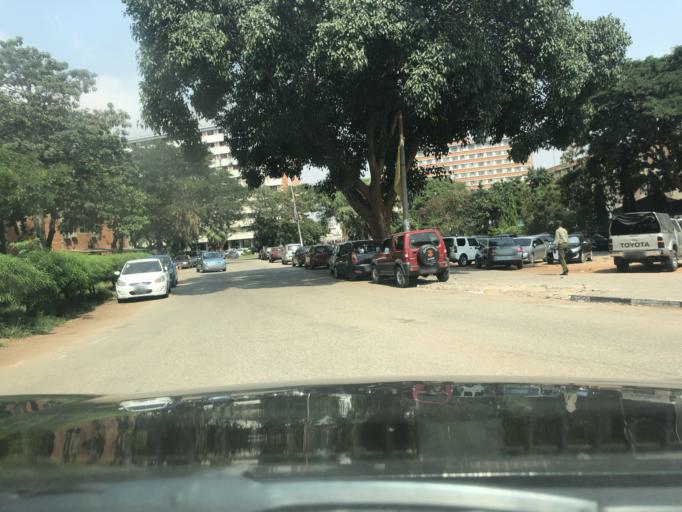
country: AO
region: Luanda
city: Luanda
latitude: -8.8273
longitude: 13.2411
